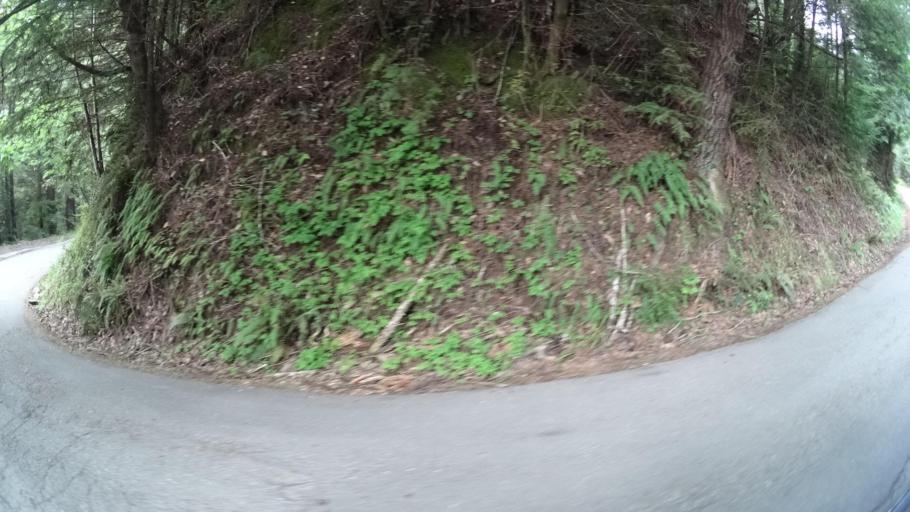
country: US
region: California
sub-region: Humboldt County
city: Redway
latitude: 40.3362
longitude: -123.9057
